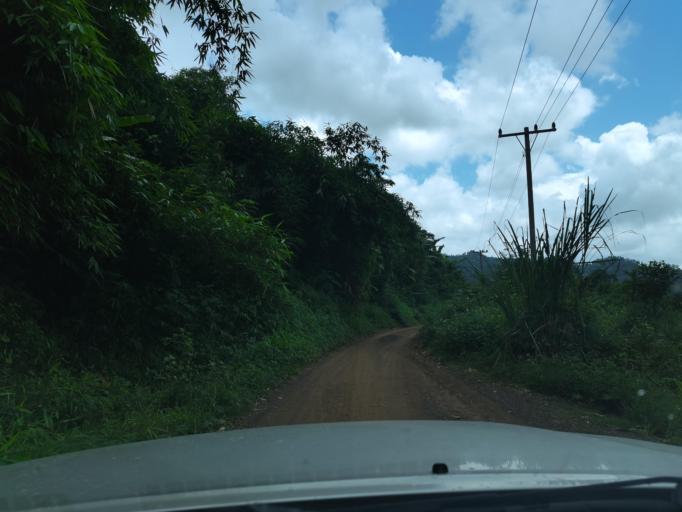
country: LA
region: Loungnamtha
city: Muang Long
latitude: 20.7558
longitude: 101.0172
